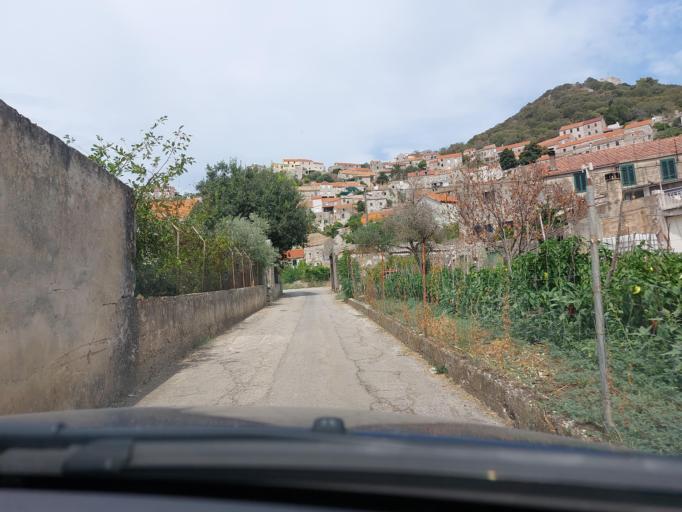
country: HR
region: Dubrovacko-Neretvanska
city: Smokvica
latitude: 42.7664
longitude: 16.8957
